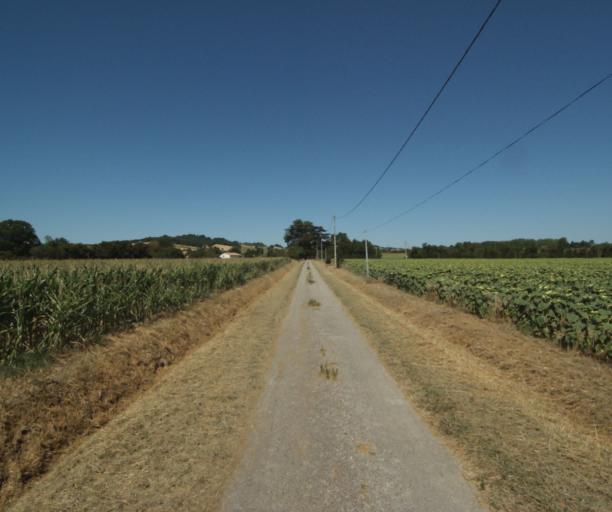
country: FR
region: Midi-Pyrenees
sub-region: Departement de la Haute-Garonne
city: Revel
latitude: 43.4950
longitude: 1.9543
